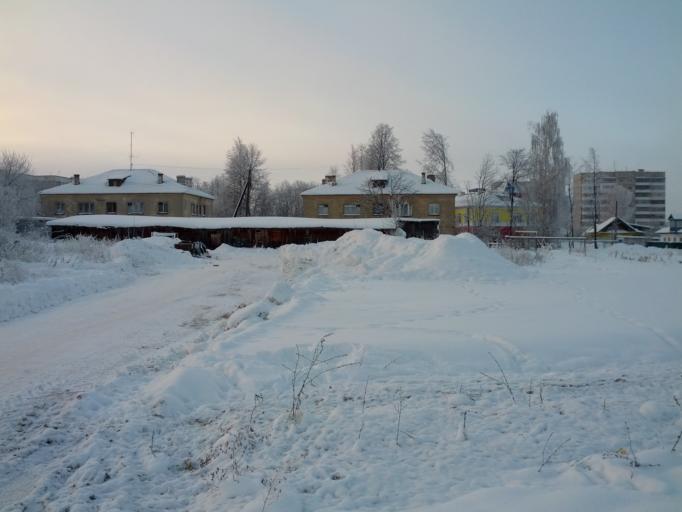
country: RU
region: Mariy-El
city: Yoshkar-Ola
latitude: 56.6460
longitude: 47.8568
